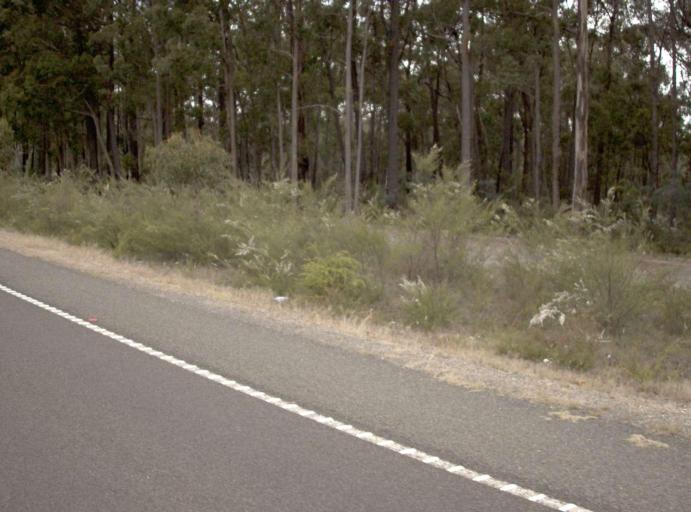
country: AU
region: Victoria
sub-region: East Gippsland
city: Lakes Entrance
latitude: -37.7182
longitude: 147.9592
